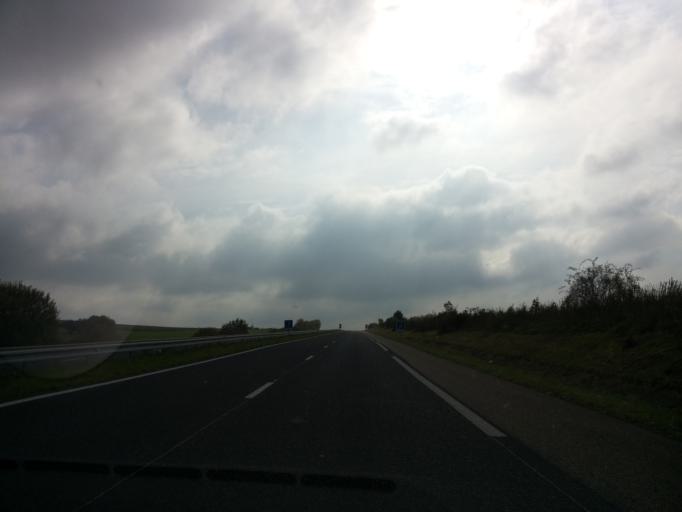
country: FR
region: Lorraine
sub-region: Departement de la Moselle
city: Solgne
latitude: 48.9392
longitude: 6.3236
